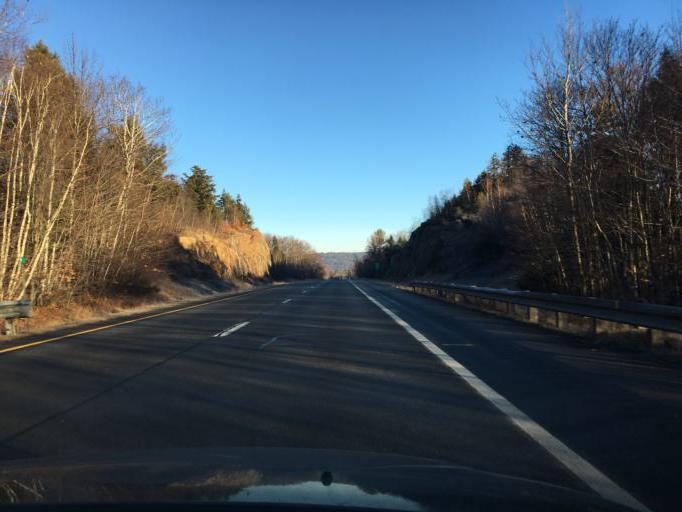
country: US
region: New Hampshire
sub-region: Belknap County
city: Sanbornton
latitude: 43.5527
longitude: -71.6166
